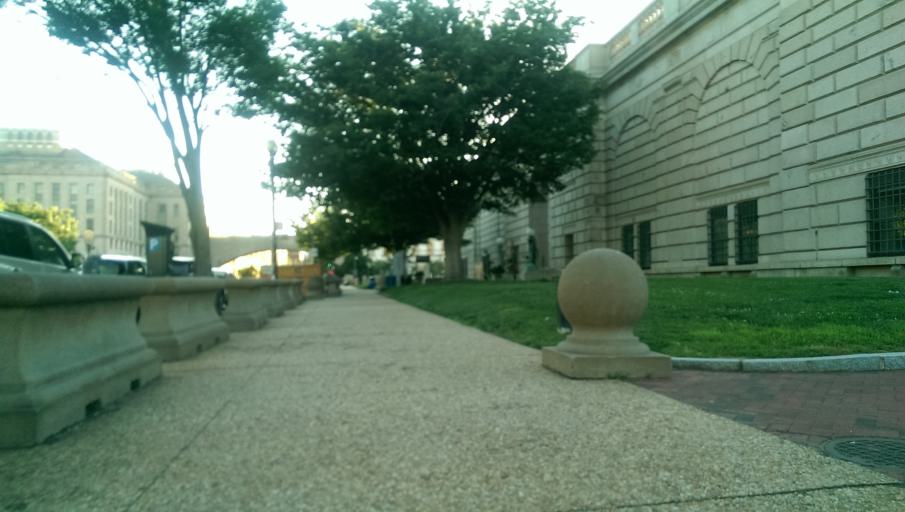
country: US
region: Washington, D.C.
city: Washington, D.C.
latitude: 38.8877
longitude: -77.0268
